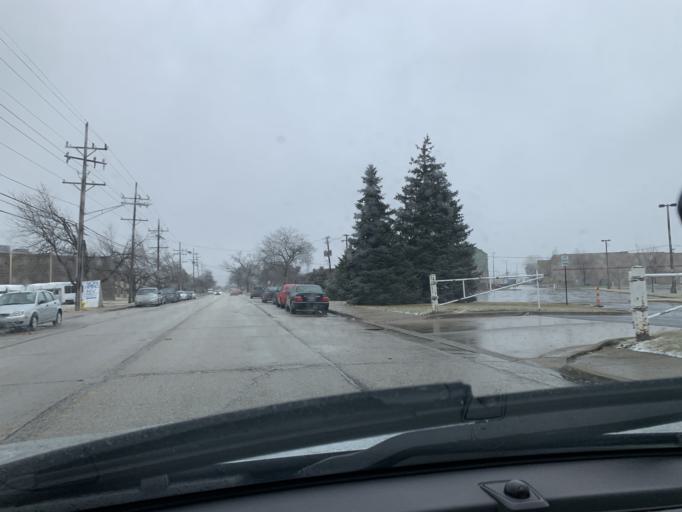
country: US
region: Illinois
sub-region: Cook County
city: Niles
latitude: 42.0157
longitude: -87.7835
